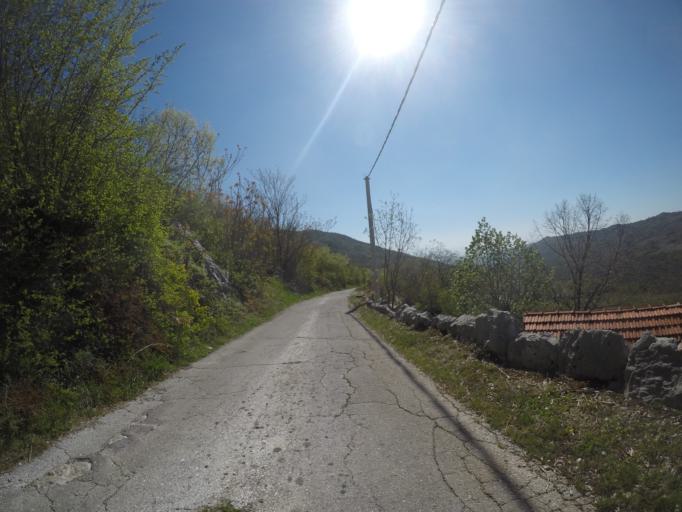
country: ME
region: Danilovgrad
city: Danilovgrad
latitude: 42.5272
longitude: 19.0417
